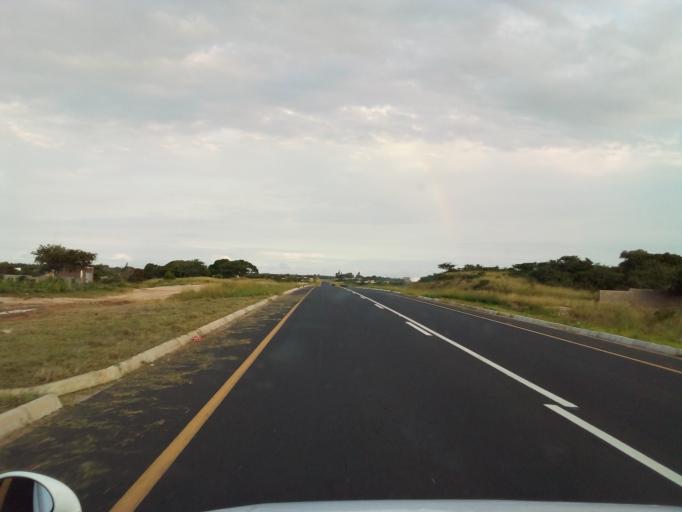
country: MZ
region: Maputo City
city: Maputo
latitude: -26.0443
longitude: 32.5690
